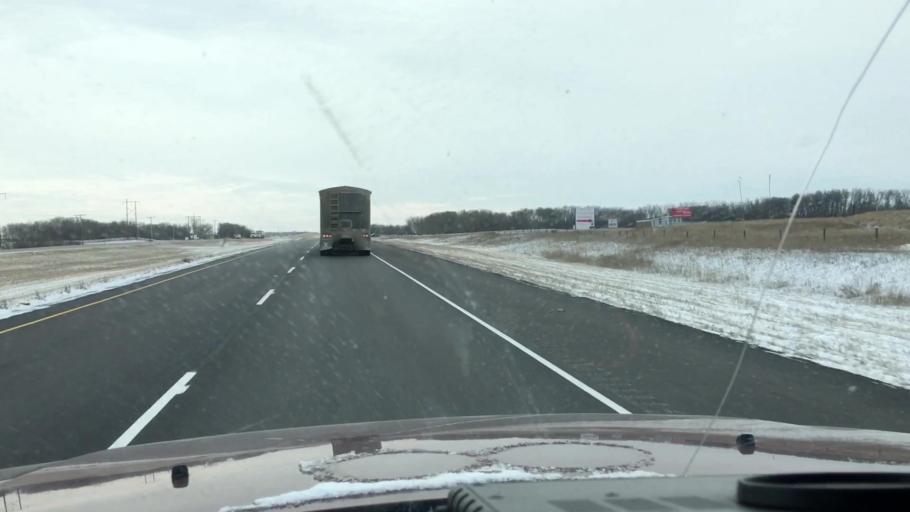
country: CA
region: Saskatchewan
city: Saskatoon
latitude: 51.9437
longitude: -106.5417
